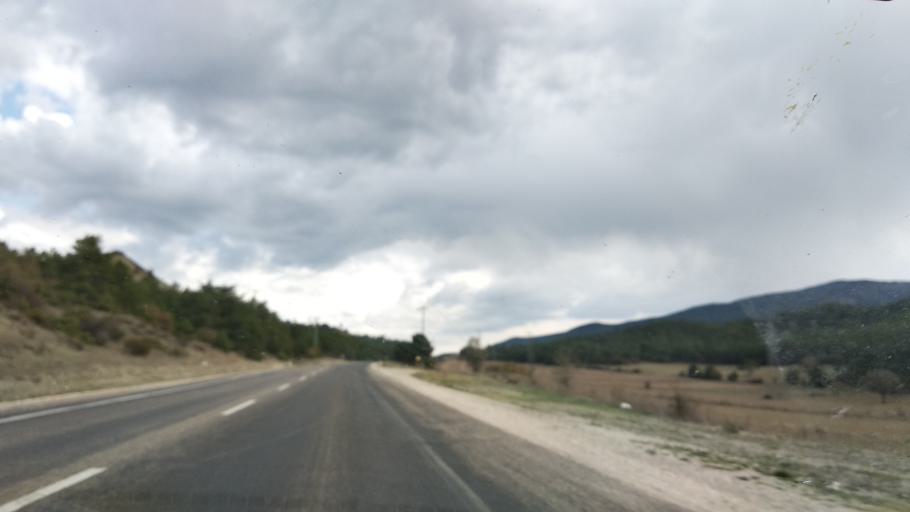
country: TR
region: Bolu
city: Mudurnu
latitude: 40.4843
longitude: 31.1823
